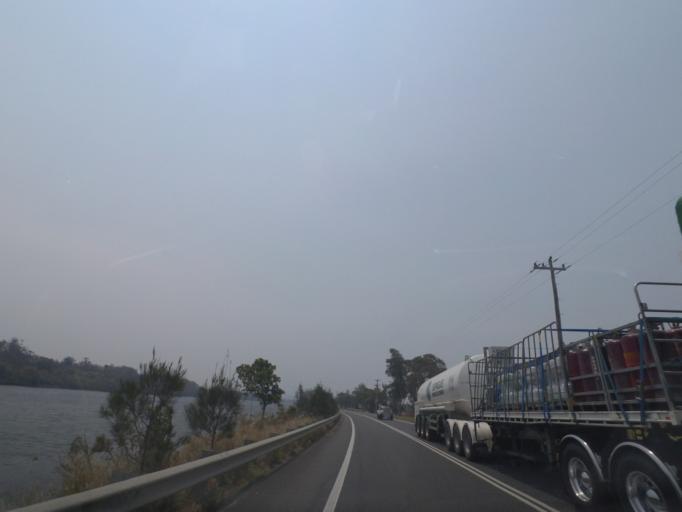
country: AU
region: New South Wales
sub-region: Richmond Valley
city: Evans Head
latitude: -28.9890
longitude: 153.4626
